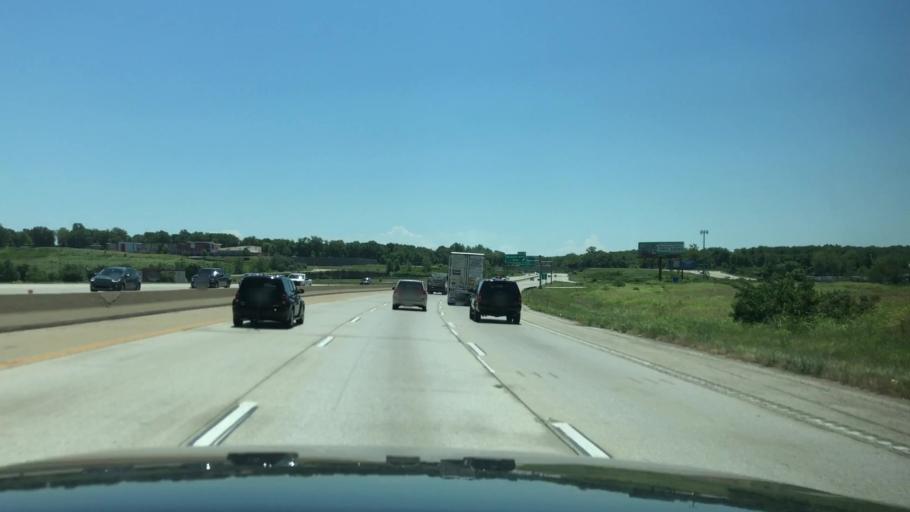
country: US
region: Missouri
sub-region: Saint Louis County
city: Bridgeton
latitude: 38.7868
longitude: -90.4204
